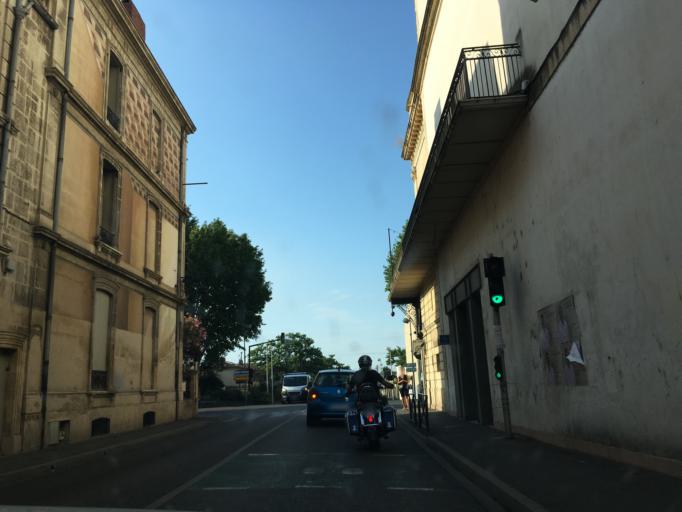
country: FR
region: Provence-Alpes-Cote d'Azur
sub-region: Departement des Bouches-du-Rhone
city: Arles
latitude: 43.6754
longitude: 4.6249
